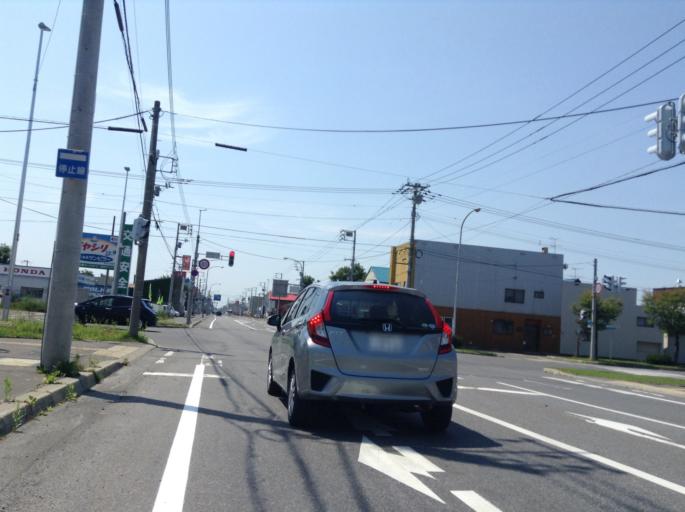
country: JP
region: Hokkaido
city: Nayoro
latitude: 44.3568
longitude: 142.4572
